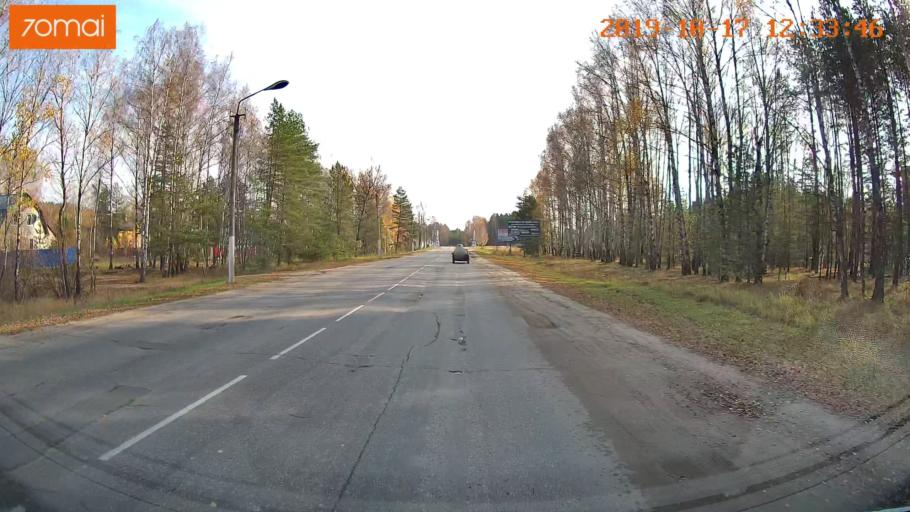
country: RU
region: Rjazan
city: Kasimov
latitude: 54.9521
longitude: 41.3573
